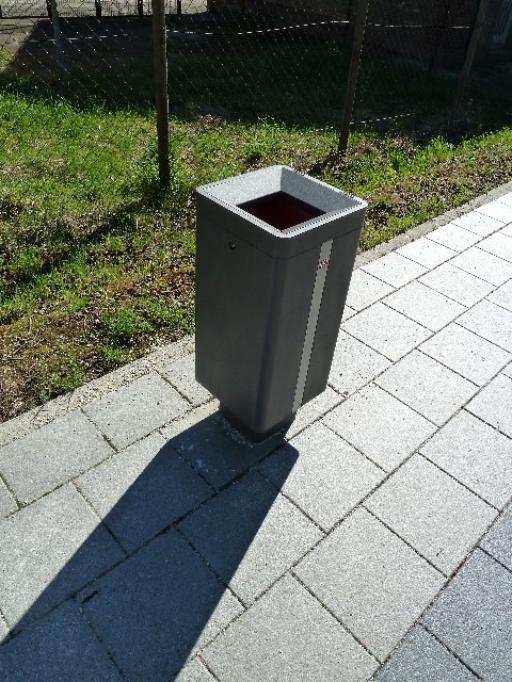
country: DE
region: Baden-Wuerttemberg
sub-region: Regierungsbezirk Stuttgart
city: Ittlingen
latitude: 49.1681
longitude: 8.9366
